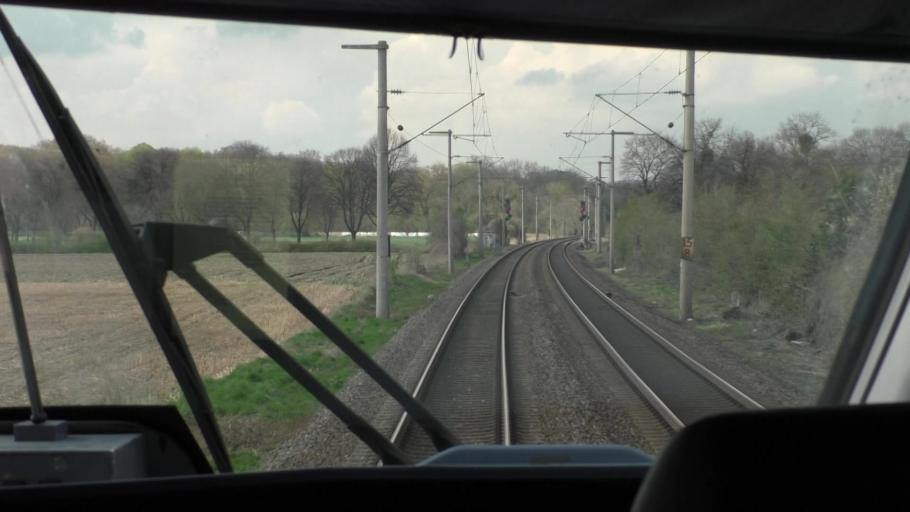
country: DE
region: North Rhine-Westphalia
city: Bruhl
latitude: 50.8195
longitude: 6.9236
